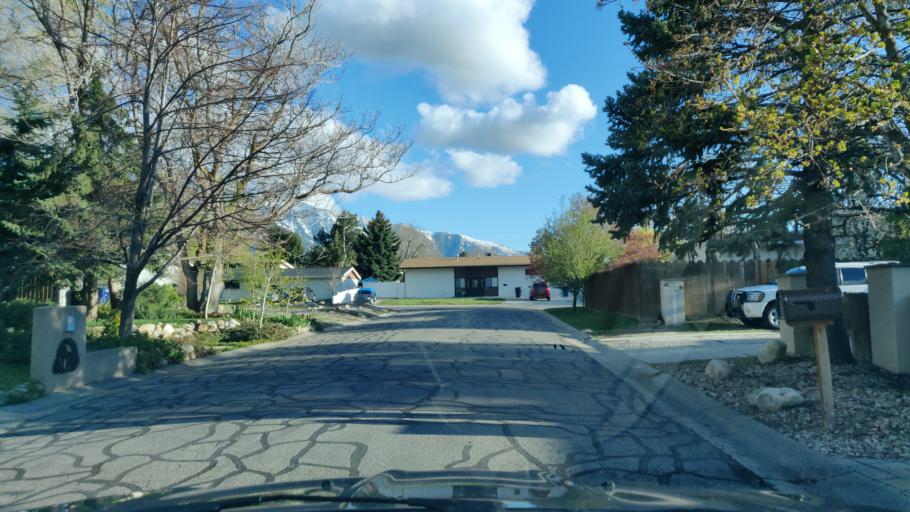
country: US
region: Utah
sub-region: Salt Lake County
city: Cottonwood Heights
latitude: 40.6232
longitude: -111.8080
